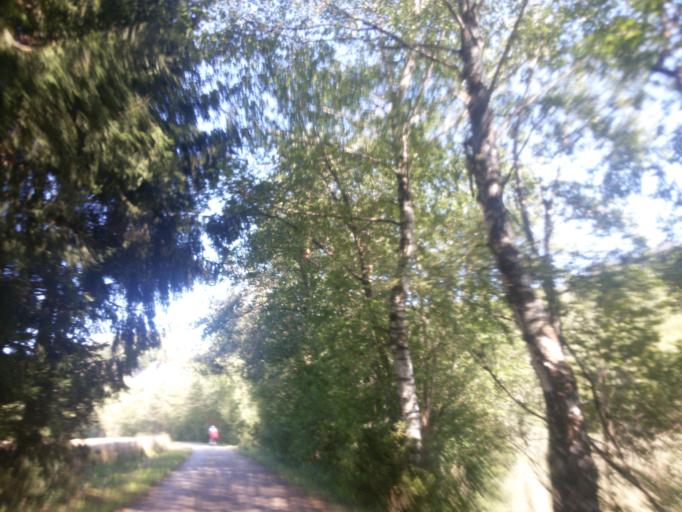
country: AT
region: Carinthia
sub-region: Politischer Bezirk Villach Land
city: Wernberg
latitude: 46.6056
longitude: 13.9095
